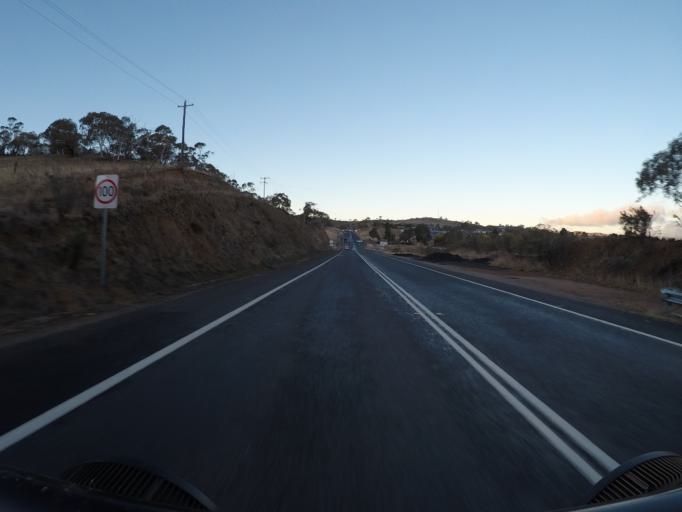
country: AU
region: New South Wales
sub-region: Snowy River
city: Jindabyne
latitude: -36.3998
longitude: 148.6535
